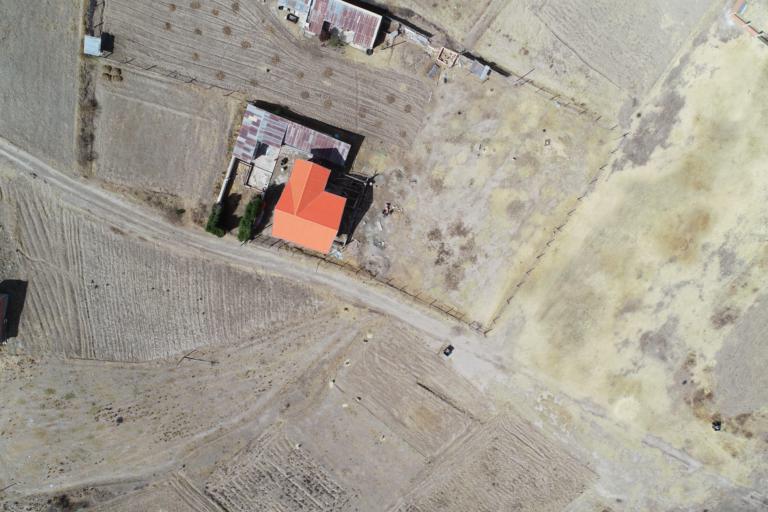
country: BO
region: La Paz
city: La Paz
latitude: -16.5982
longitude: -68.1282
